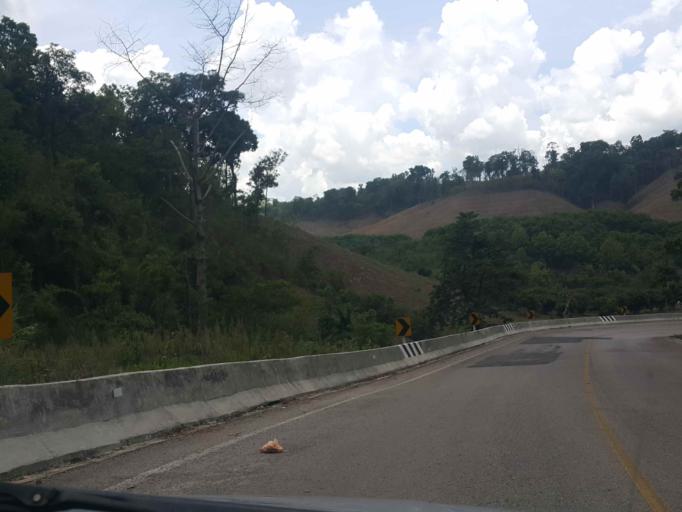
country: TH
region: Phayao
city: Chiang Muan
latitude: 18.9255
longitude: 100.1036
